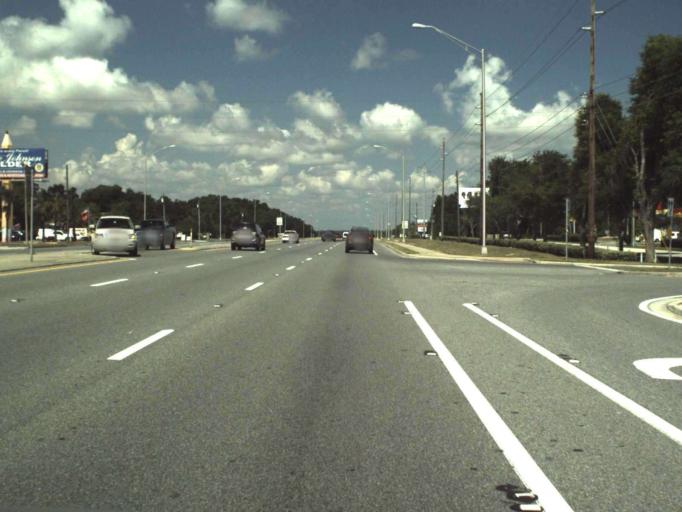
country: US
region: Florida
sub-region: Lake County
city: Mount Dora
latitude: 28.8242
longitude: -81.6466
